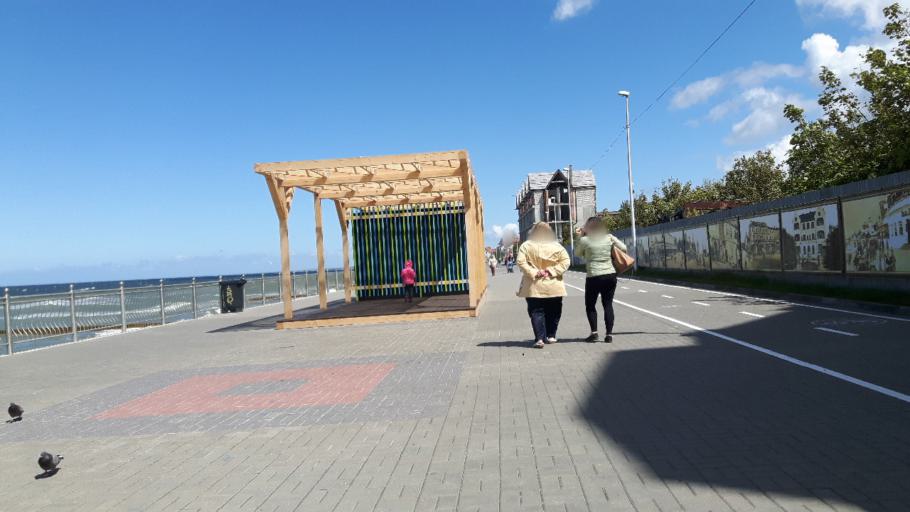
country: RU
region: Kaliningrad
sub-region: Zelenogradskiy Rayon
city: Zelenogradsk
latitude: 54.9623
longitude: 20.4760
